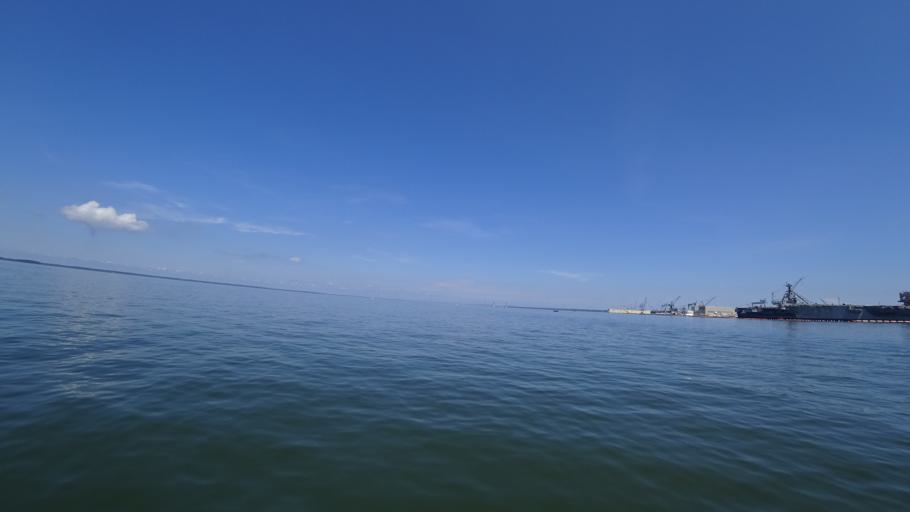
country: US
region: Virginia
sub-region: City of Newport News
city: Newport News
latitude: 36.9740
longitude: -76.4406
